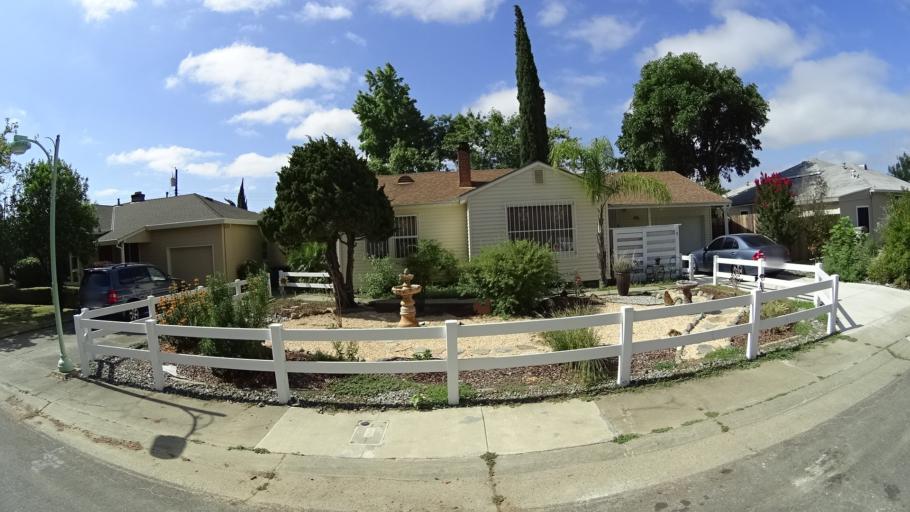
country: US
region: California
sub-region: Sacramento County
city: Parkway
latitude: 38.5322
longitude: -121.4841
